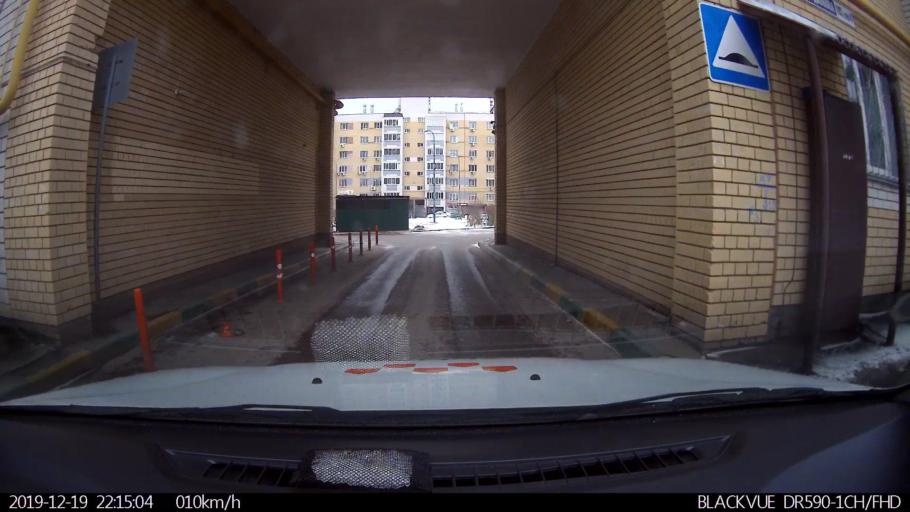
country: RU
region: Nizjnij Novgorod
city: Afonino
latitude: 56.3036
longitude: 44.0747
